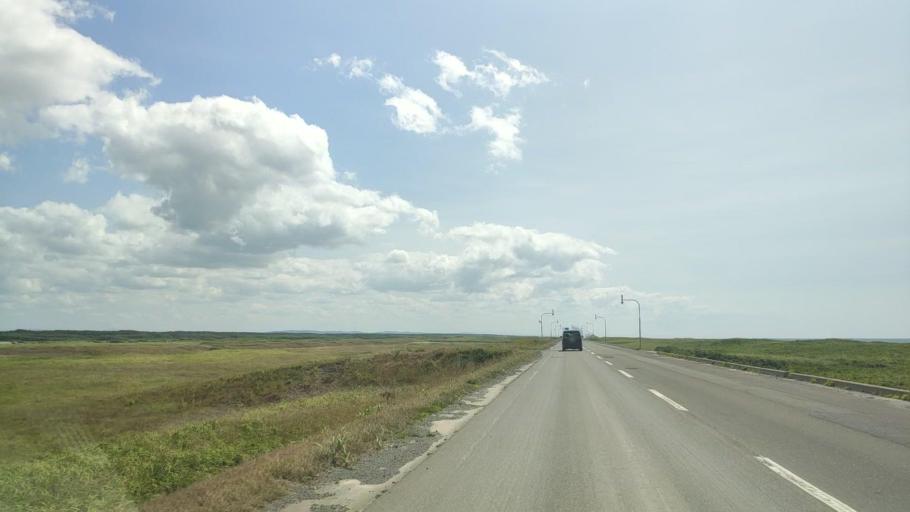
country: JP
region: Hokkaido
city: Makubetsu
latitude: 45.0226
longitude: 141.6700
